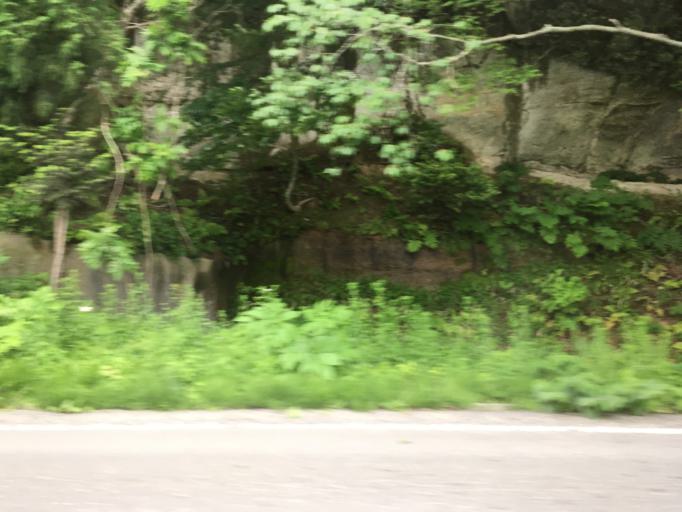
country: JP
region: Fukushima
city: Namie
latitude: 37.4821
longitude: 141.0140
